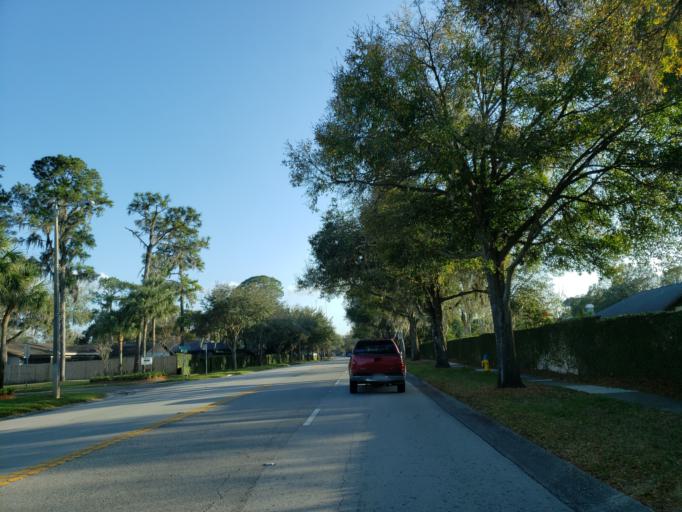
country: US
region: Florida
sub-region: Hillsborough County
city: Bloomingdale
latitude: 27.8814
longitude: -82.2664
